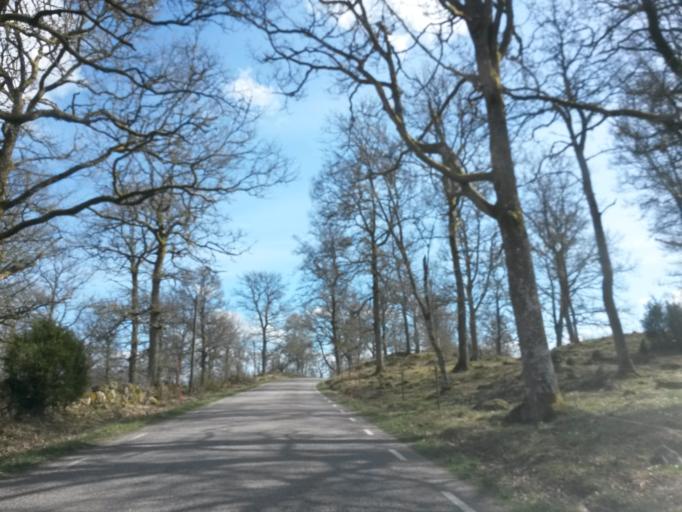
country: SE
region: Vaestra Goetaland
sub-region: Vargarda Kommun
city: Jonstorp
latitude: 57.9996
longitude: 12.7604
